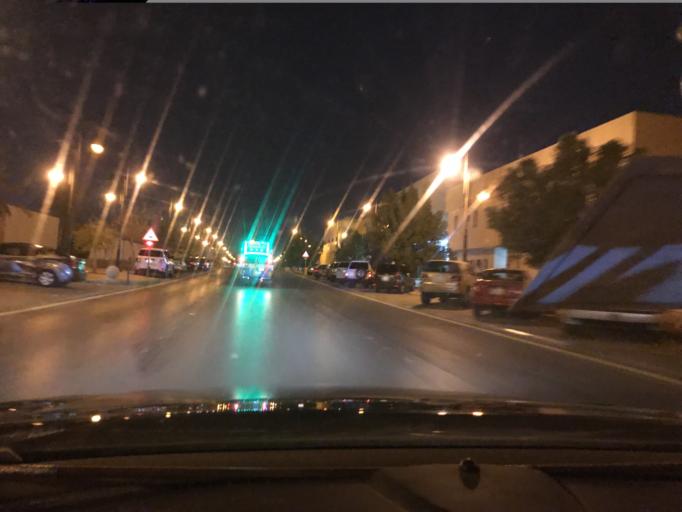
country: SA
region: Ar Riyad
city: Riyadh
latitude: 24.7422
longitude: 46.7692
